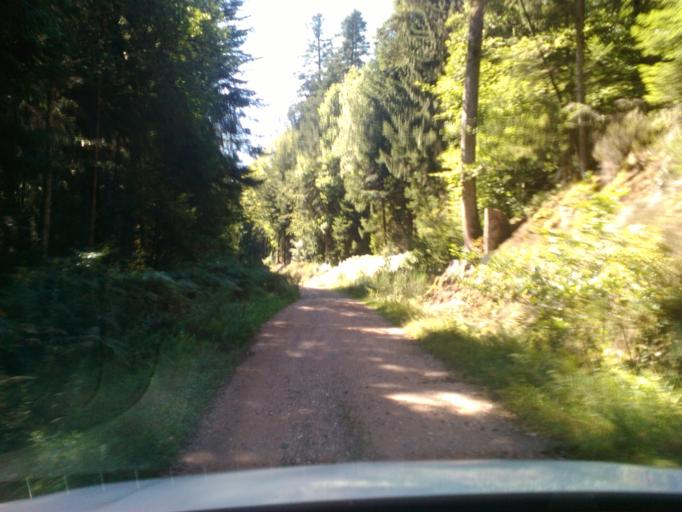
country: FR
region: Lorraine
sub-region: Departement des Vosges
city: Moyenmoutier
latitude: 48.4054
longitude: 6.9084
